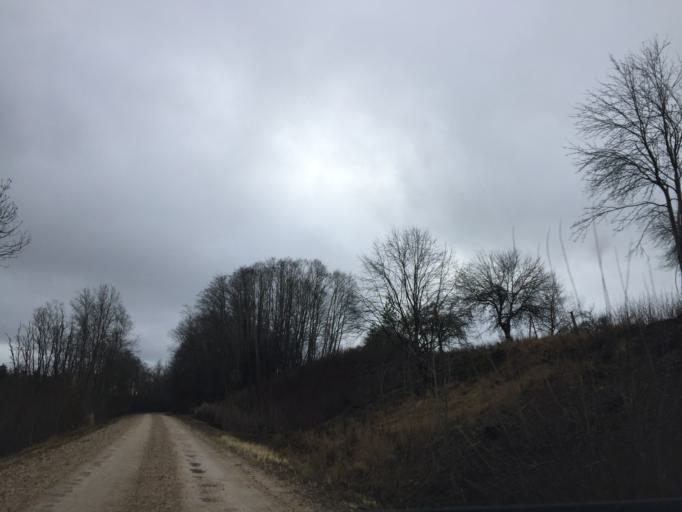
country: LV
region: Broceni
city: Broceni
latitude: 56.6869
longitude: 22.5579
